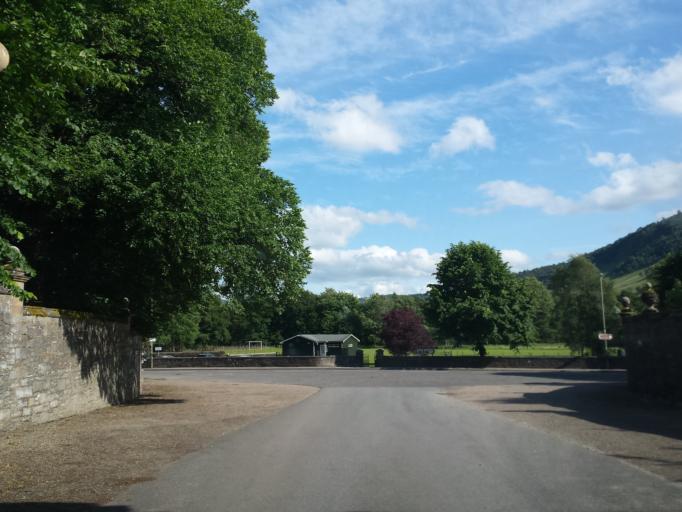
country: GB
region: Scotland
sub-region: Perth and Kinross
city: Pitlochry
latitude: 56.7669
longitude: -3.8456
